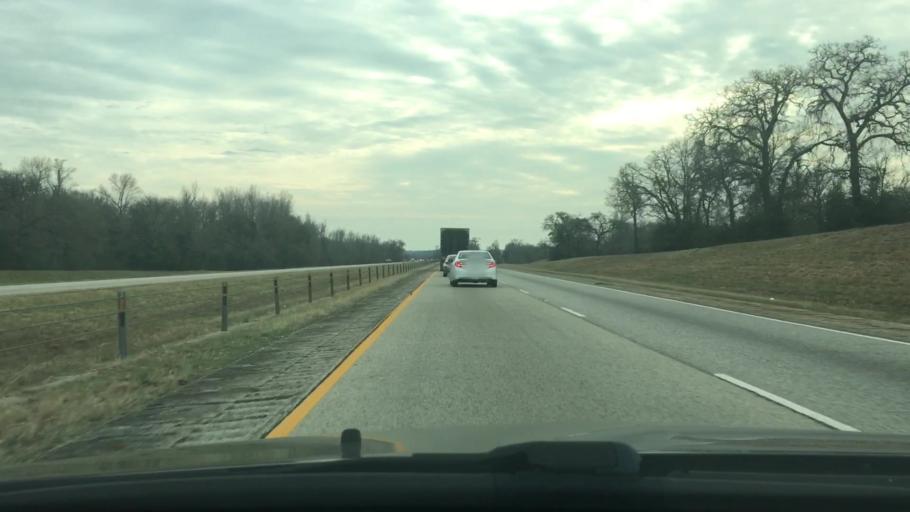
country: US
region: Texas
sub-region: Leon County
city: Centerville
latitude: 31.2201
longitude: -95.9960
